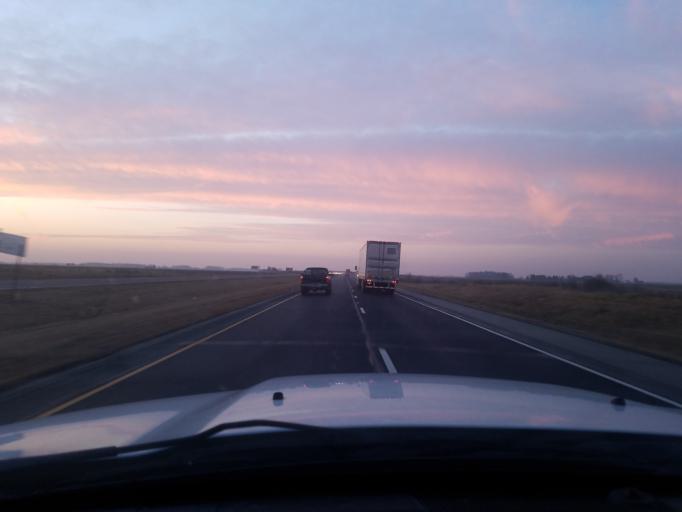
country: US
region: Indiana
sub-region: Huntington County
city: Markle
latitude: 40.8868
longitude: -85.3456
